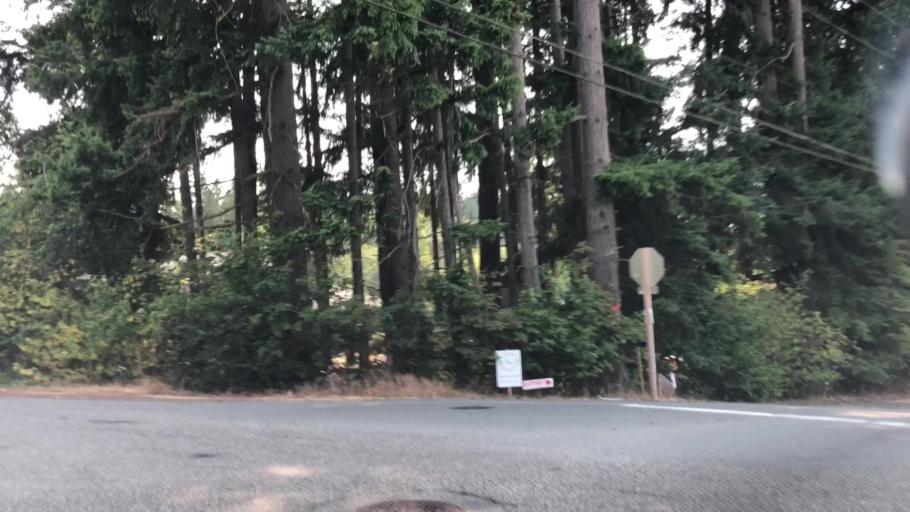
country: US
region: Washington
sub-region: Snohomish County
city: Alderwood Manor
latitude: 47.8083
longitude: -122.2542
